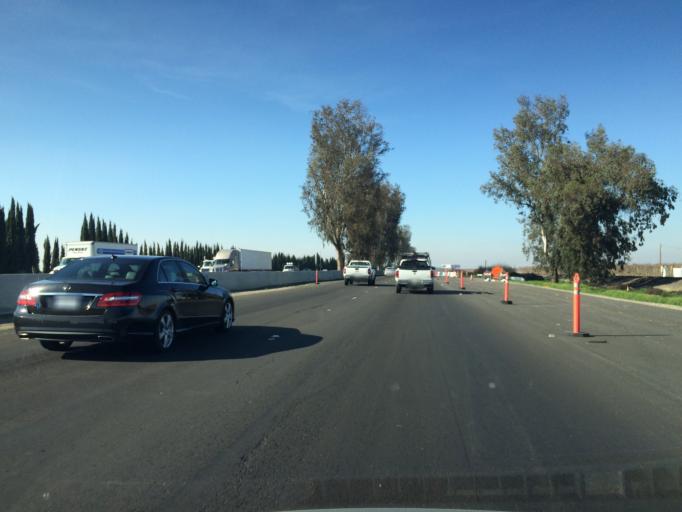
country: US
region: California
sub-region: Tulare County
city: London
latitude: 36.4654
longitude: -119.4965
